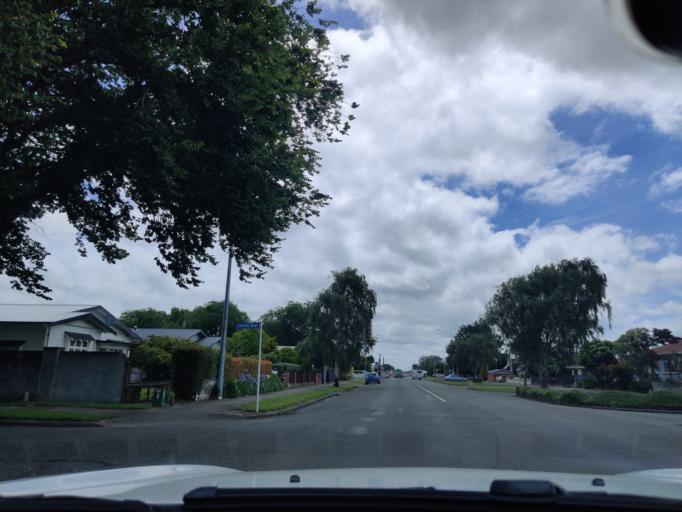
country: NZ
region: Manawatu-Wanganui
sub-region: Palmerston North City
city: Palmerston North
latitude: -40.3555
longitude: 175.6281
